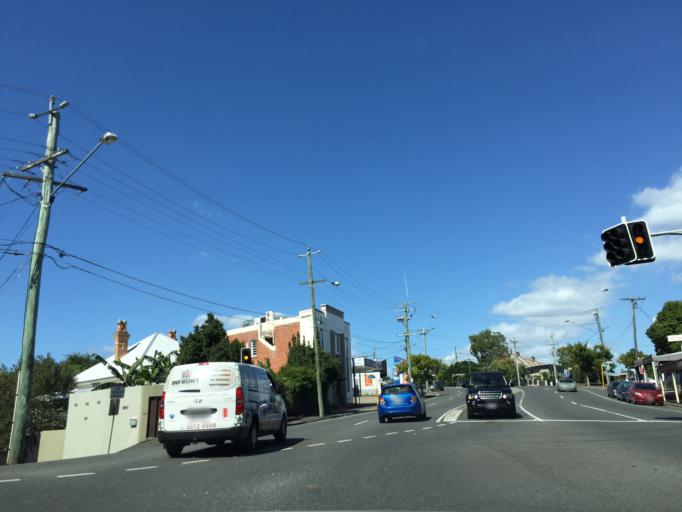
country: AU
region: Queensland
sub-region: Brisbane
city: Milton
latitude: -27.4545
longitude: 153.0067
